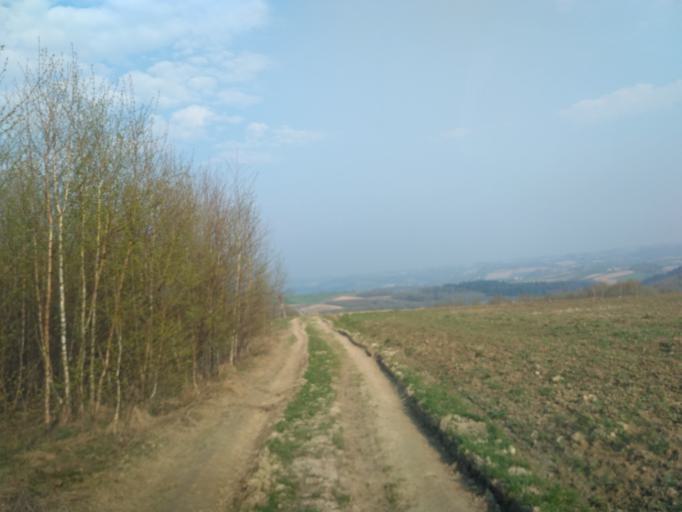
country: PL
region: Subcarpathian Voivodeship
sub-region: Powiat ropczycko-sedziszowski
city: Wielopole Skrzynskie
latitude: 49.9077
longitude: 21.5795
